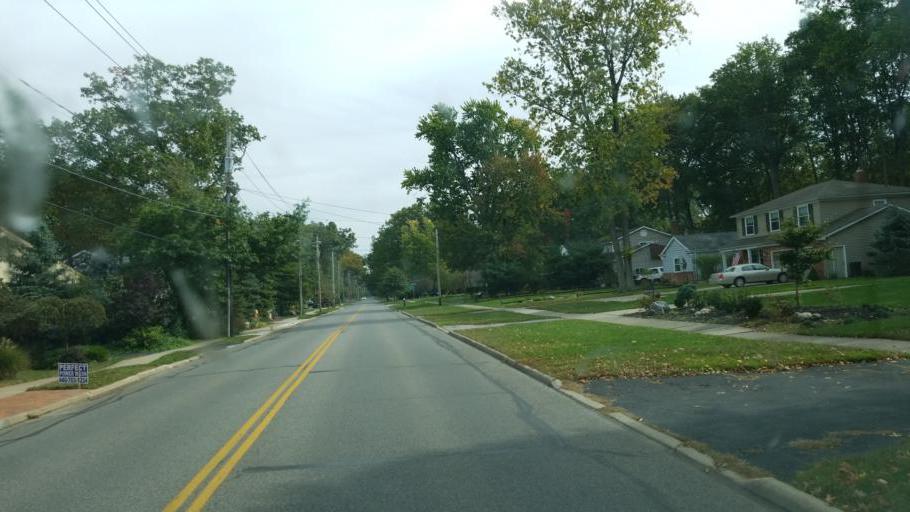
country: US
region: Ohio
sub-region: Cuyahoga County
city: Bay Village
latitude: 41.5033
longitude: -81.9673
